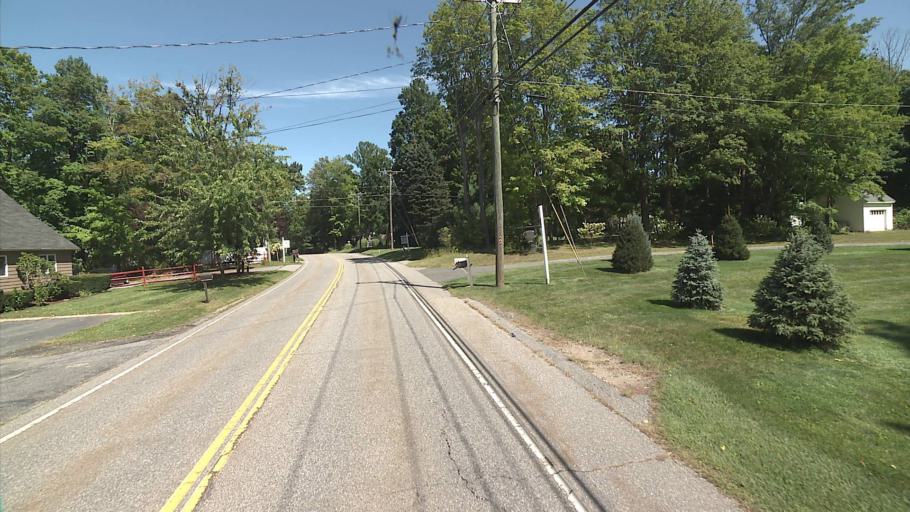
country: US
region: Connecticut
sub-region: Litchfield County
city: Litchfield
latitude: 41.7024
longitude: -73.2331
